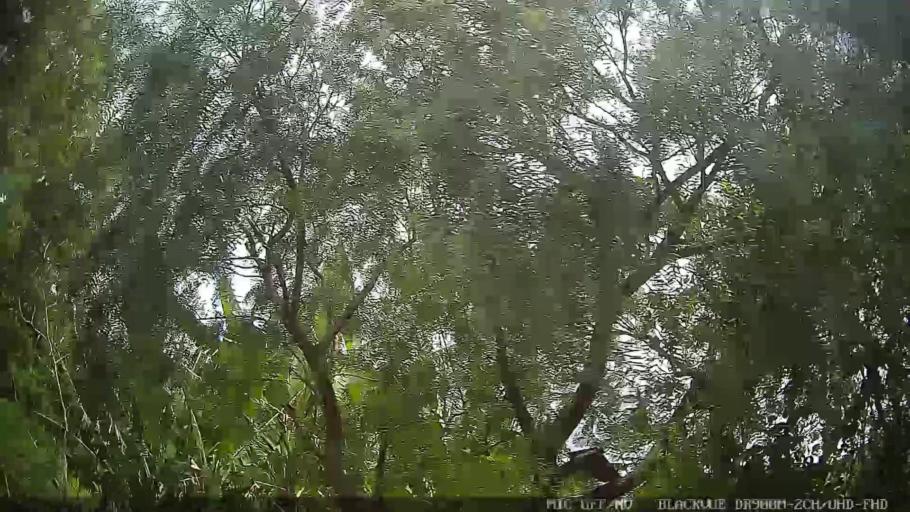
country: BR
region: Sao Paulo
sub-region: Serra Negra
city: Serra Negra
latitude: -22.5949
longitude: -46.7171
